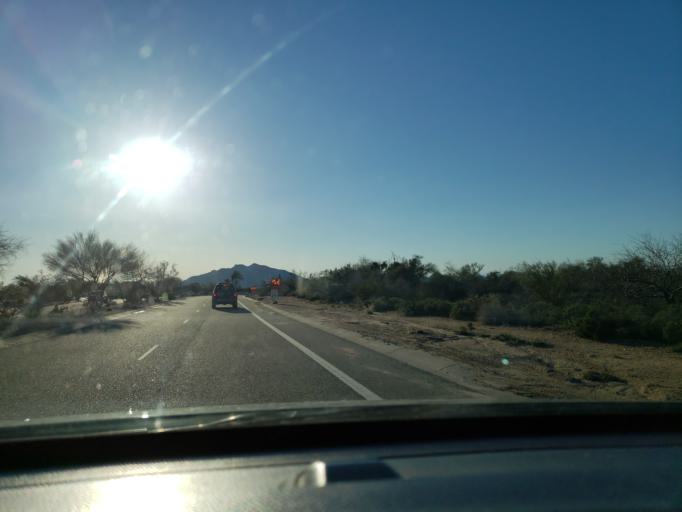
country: US
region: Arizona
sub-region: Maricopa County
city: Carefree
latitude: 33.8253
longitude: -111.8720
